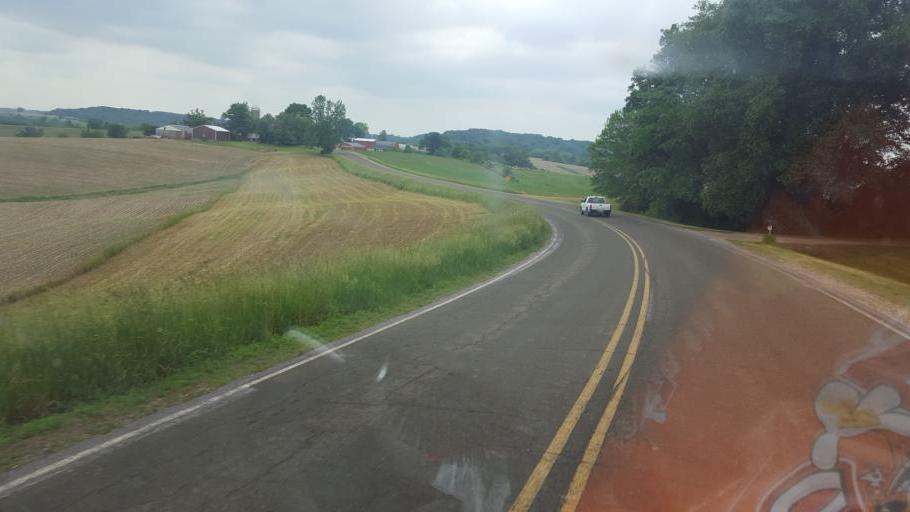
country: US
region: Wisconsin
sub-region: Vernon County
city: Hillsboro
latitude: 43.6480
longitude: -90.2670
